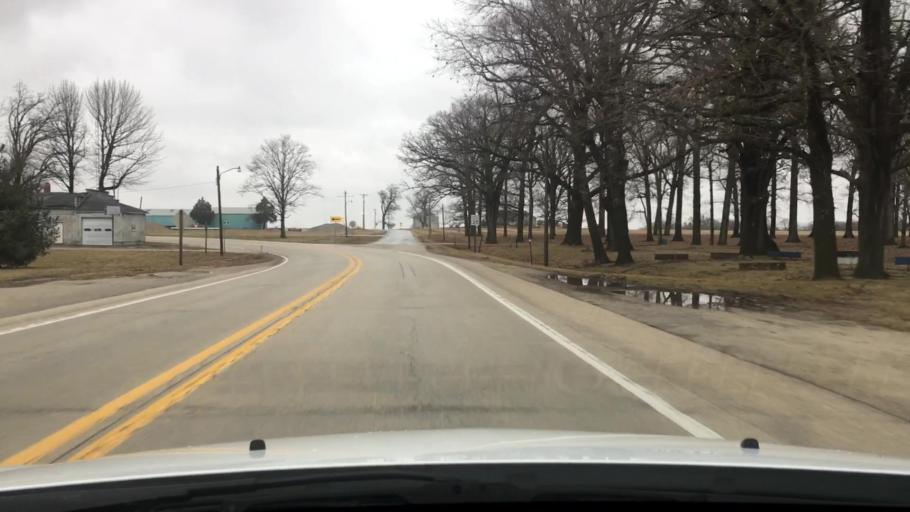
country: US
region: Illinois
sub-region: Iroquois County
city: Sheldon
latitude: 40.8276
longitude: -87.5817
